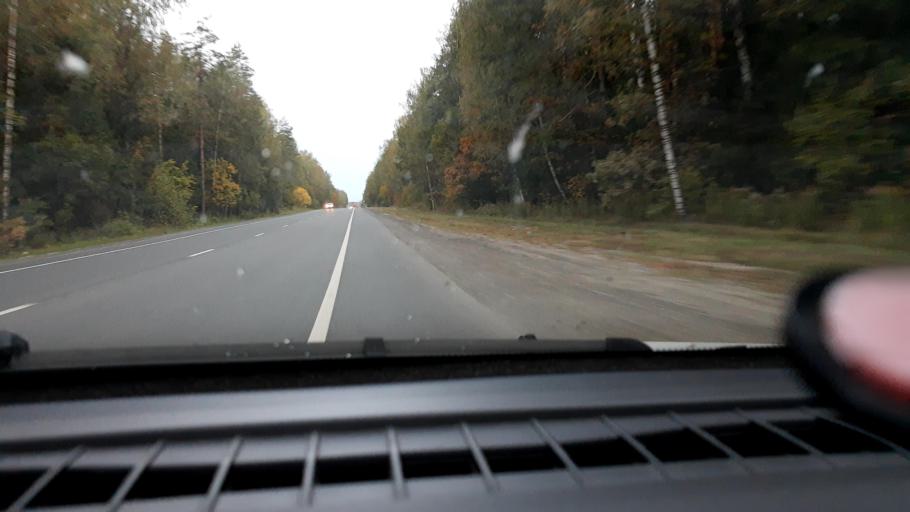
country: RU
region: Vladimir
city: Orgtrud
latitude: 56.2062
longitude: 40.7075
